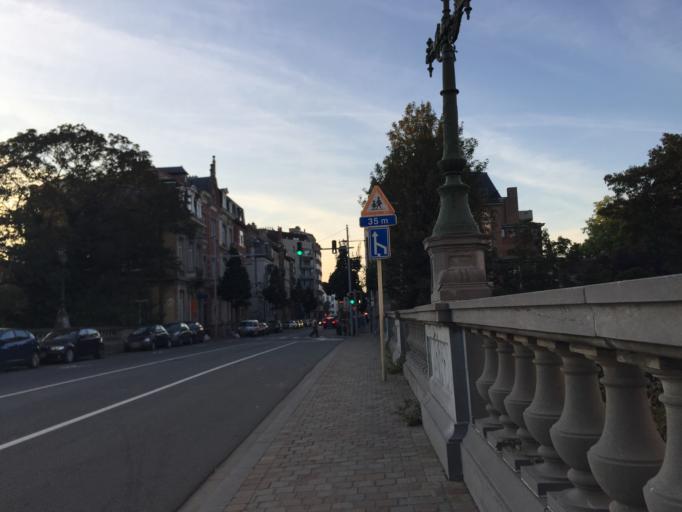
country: BE
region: Brussels Capital
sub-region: Bruxelles-Capitale
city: Brussels
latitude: 50.8314
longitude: 4.3771
